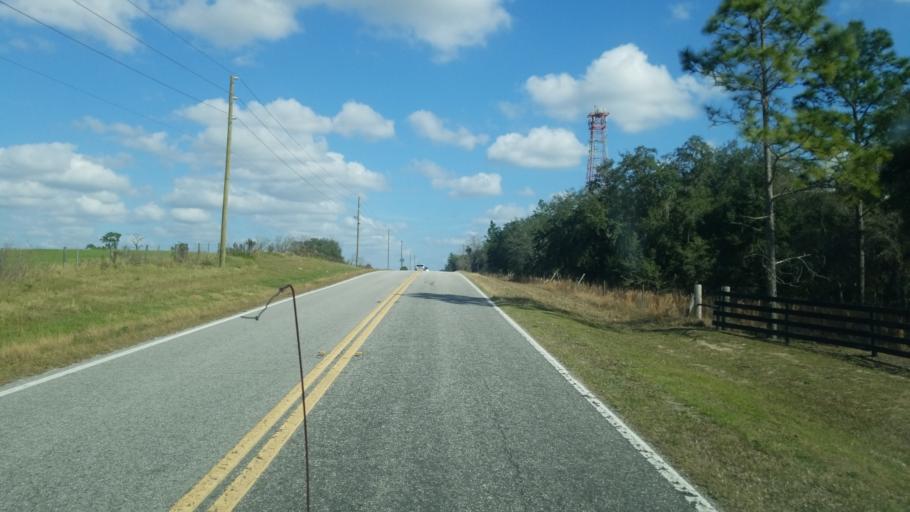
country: US
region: Florida
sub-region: Citrus County
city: Floral City
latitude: 28.7121
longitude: -82.3422
